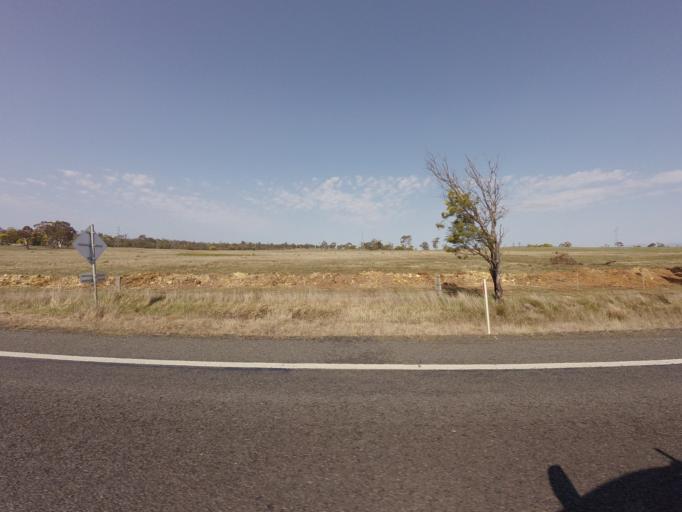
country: AU
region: Tasmania
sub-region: Northern Midlands
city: Evandale
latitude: -41.8351
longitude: 147.4551
